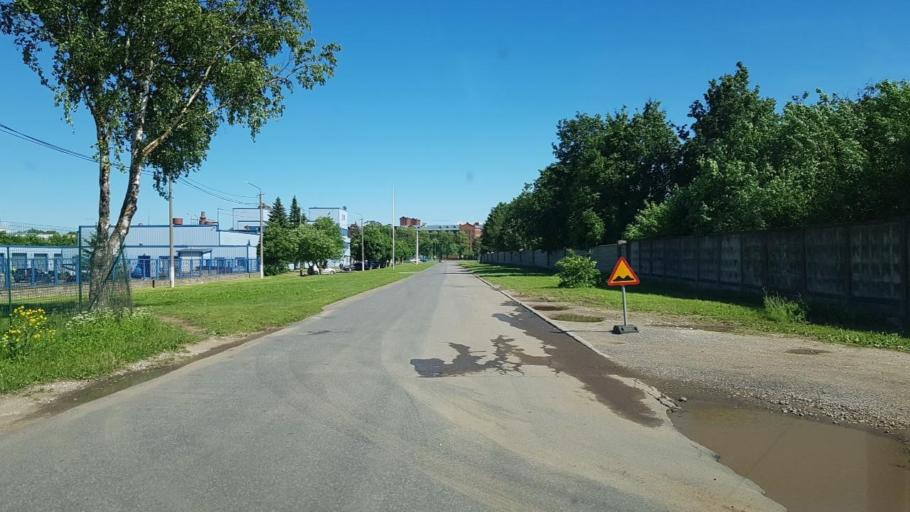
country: EE
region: Ida-Virumaa
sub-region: Narva linn
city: Narva
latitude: 59.3599
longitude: 28.1809
